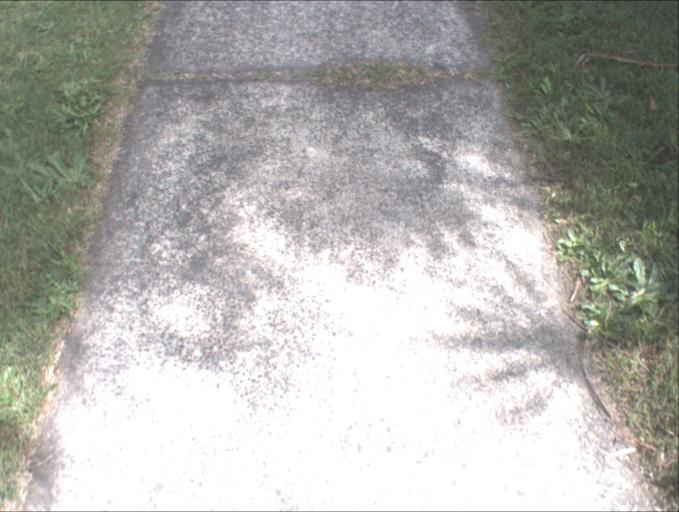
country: AU
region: Queensland
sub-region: Logan
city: Park Ridge South
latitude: -27.6779
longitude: 153.0343
